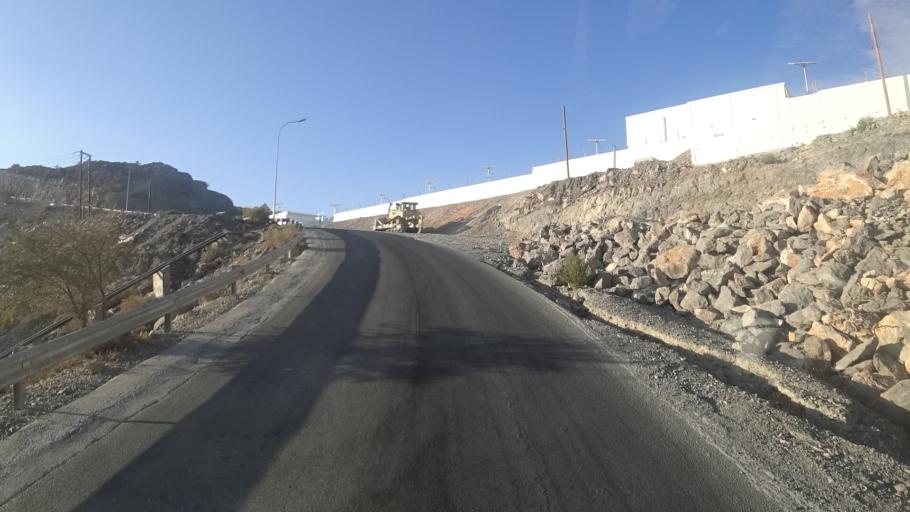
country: OM
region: Muhafazat ad Dakhiliyah
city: Izki
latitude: 23.0940
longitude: 57.6827
